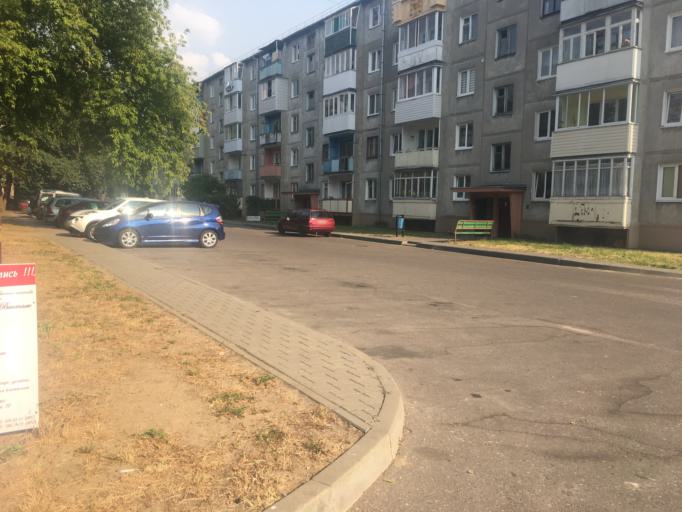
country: BY
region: Grodnenskaya
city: Hrodna
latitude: 53.6668
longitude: 23.8032
